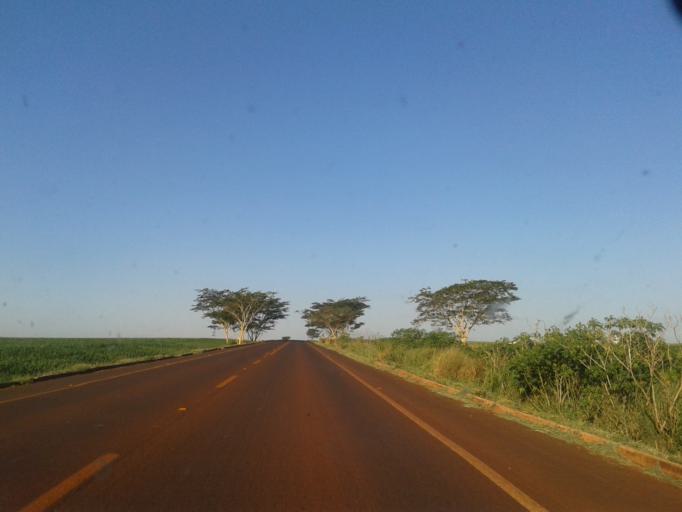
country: BR
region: Minas Gerais
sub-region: Capinopolis
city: Capinopolis
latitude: -18.6994
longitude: -49.6479
